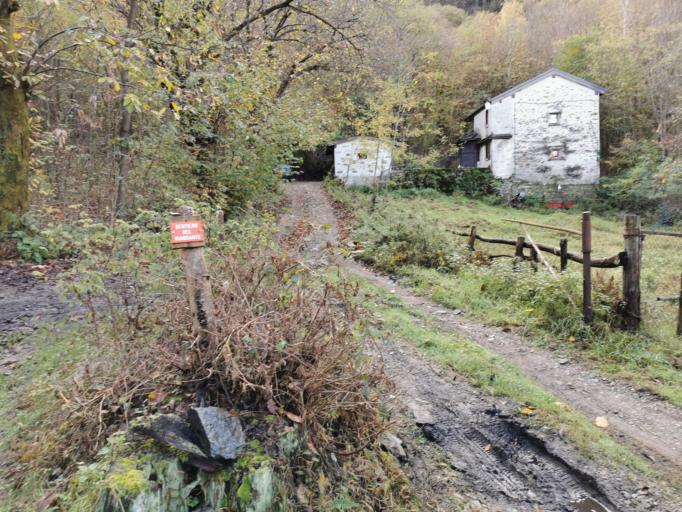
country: IT
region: Lombardy
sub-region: Provincia di Sondrio
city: Piantedo
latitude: 46.1316
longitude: 9.4272
